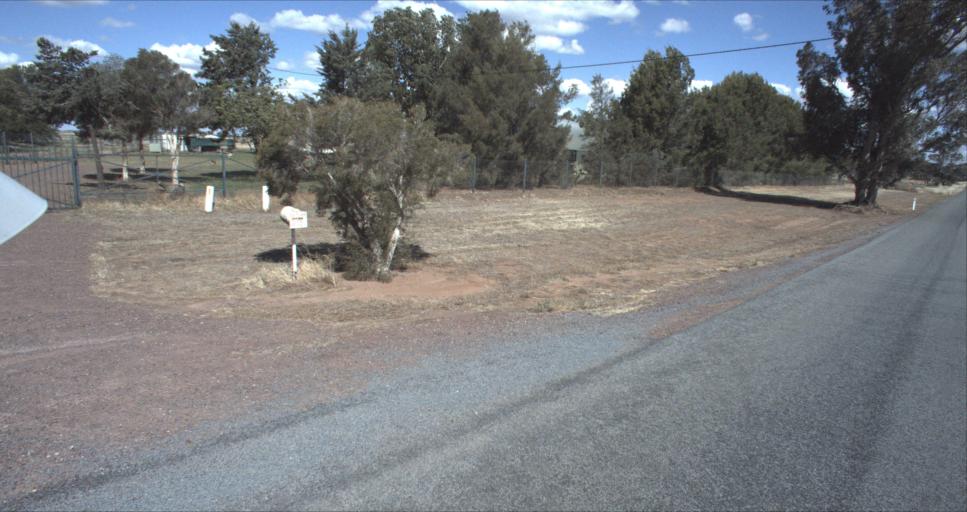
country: AU
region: New South Wales
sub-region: Leeton
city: Leeton
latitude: -34.4844
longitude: 146.2485
